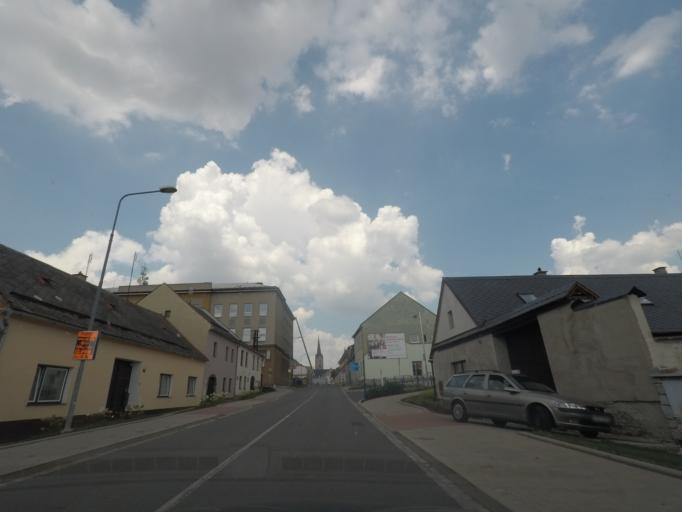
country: CZ
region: Olomoucky
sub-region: Okres Sumperk
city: Mohelnice
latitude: 49.7736
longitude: 16.9181
